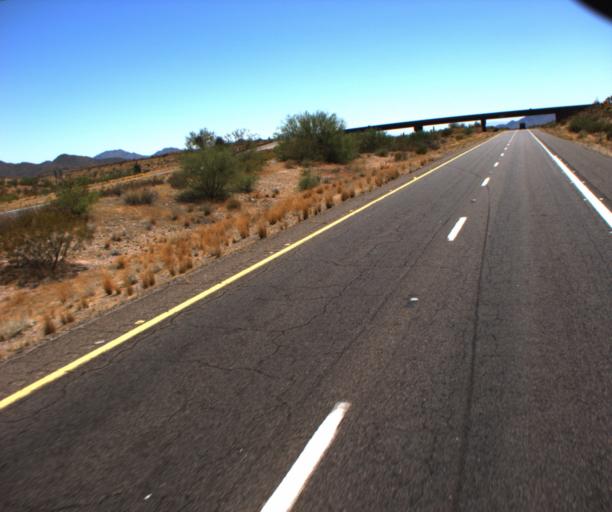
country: US
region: Arizona
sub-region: Maricopa County
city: Rio Verde
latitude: 33.6294
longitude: -111.5572
